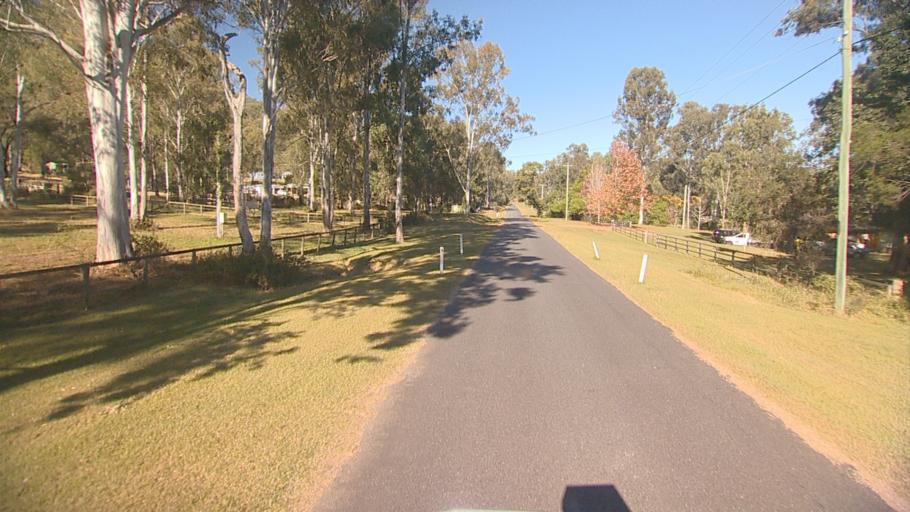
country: AU
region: Queensland
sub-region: Logan
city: Windaroo
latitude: -27.7812
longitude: 153.1480
